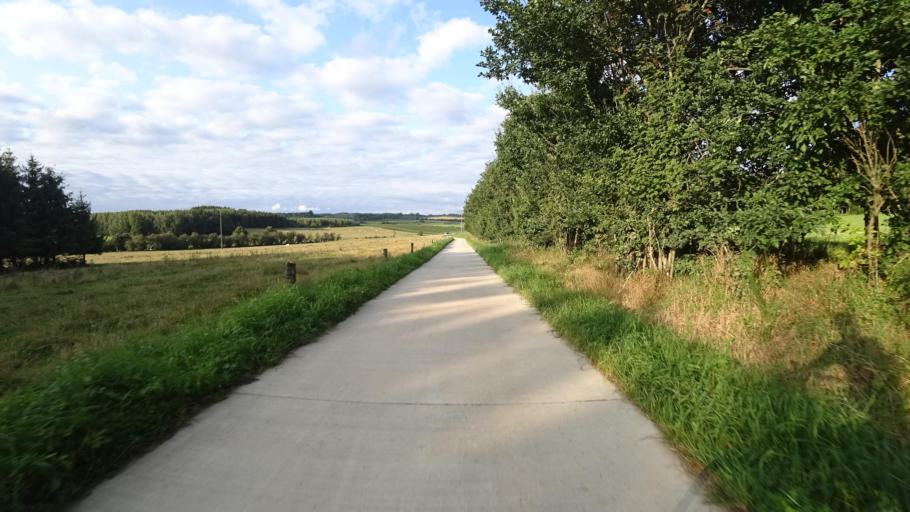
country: BE
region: Wallonia
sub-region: Province du Luxembourg
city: Neufchateau
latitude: 49.8483
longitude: 5.3494
